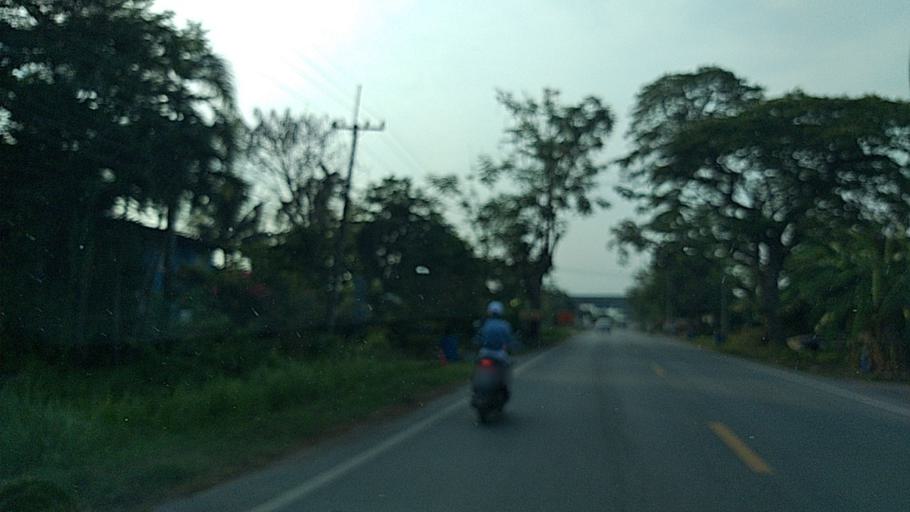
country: TH
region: Sara Buri
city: Saraburi
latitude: 14.4629
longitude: 100.9420
